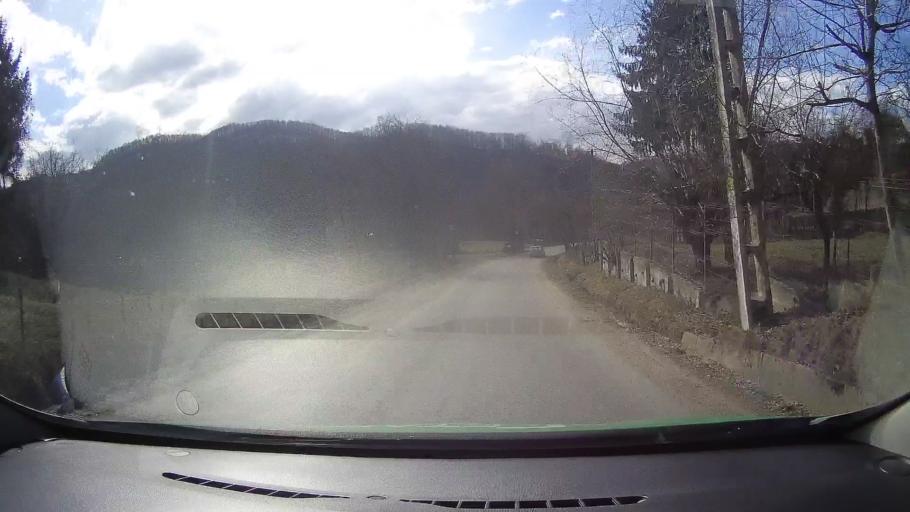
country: RO
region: Dambovita
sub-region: Comuna Varfuri
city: Varfuri
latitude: 45.0913
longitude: 25.5072
